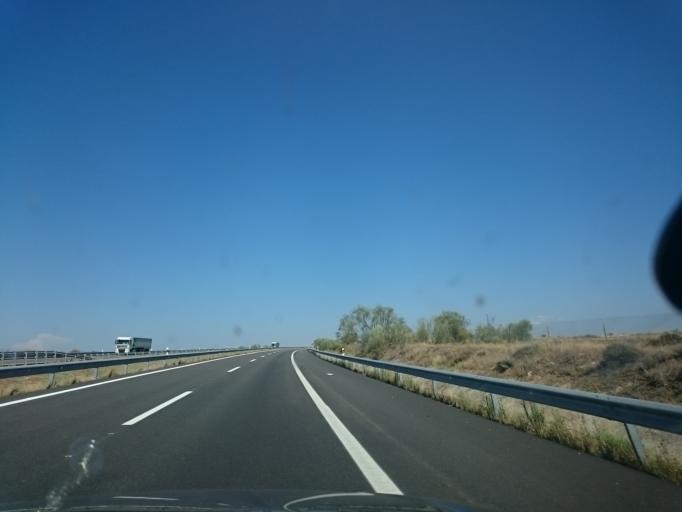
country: ES
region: Aragon
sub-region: Provincia de Zaragoza
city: Mequinensa / Mequinenza
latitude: 41.4686
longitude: 0.2536
